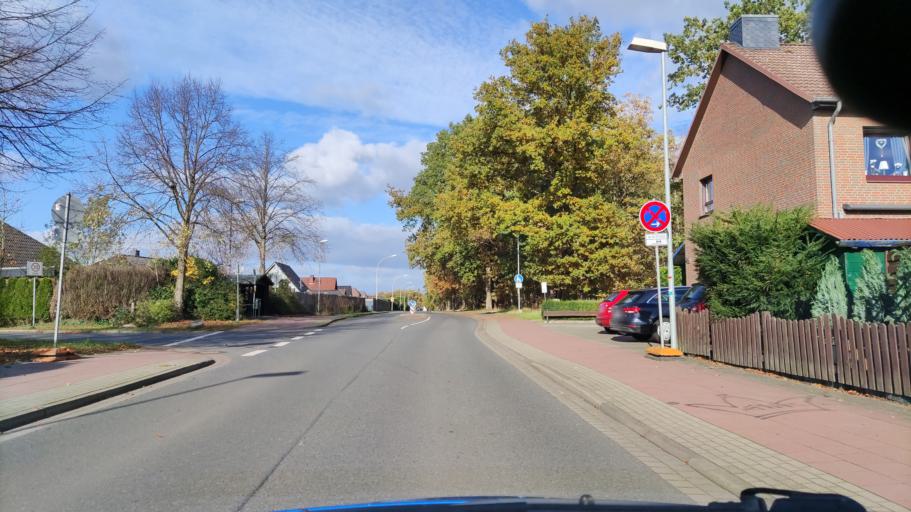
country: DE
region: Lower Saxony
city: Munster
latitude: 53.0037
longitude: 10.0887
